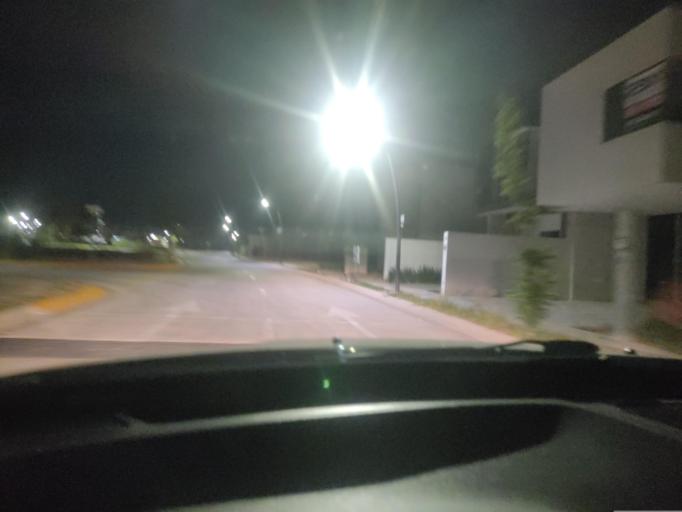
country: MX
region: Guanajuato
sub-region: Leon
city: Ladrilleras del Refugio
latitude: 21.0850
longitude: -101.5629
